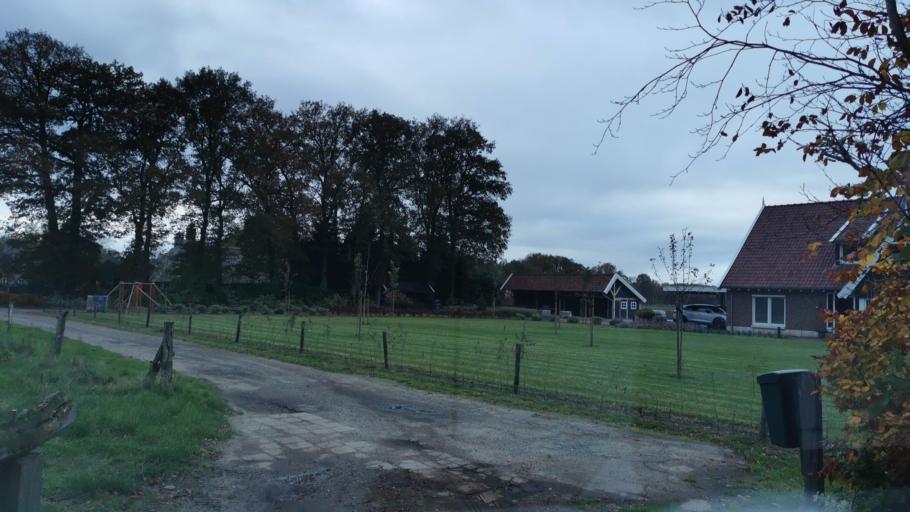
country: DE
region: North Rhine-Westphalia
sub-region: Regierungsbezirk Munster
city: Gronau
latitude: 52.2388
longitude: 7.0580
